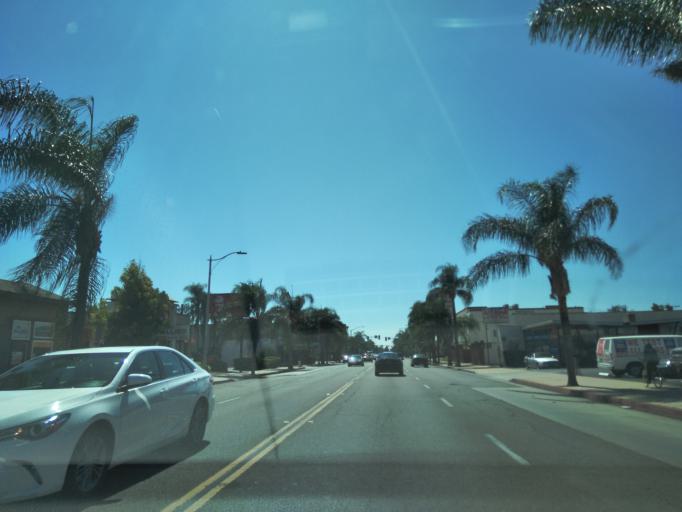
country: US
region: California
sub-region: Orange County
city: Santa Ana
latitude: 33.7305
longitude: -117.8679
